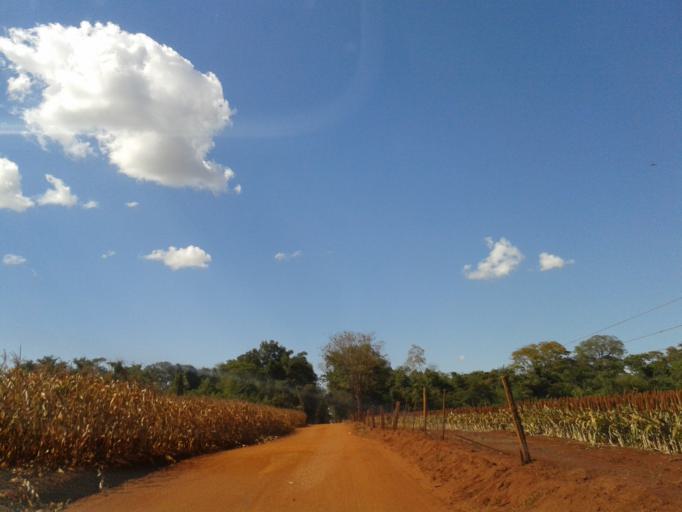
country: BR
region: Minas Gerais
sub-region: Capinopolis
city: Capinopolis
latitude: -18.6198
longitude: -49.4925
